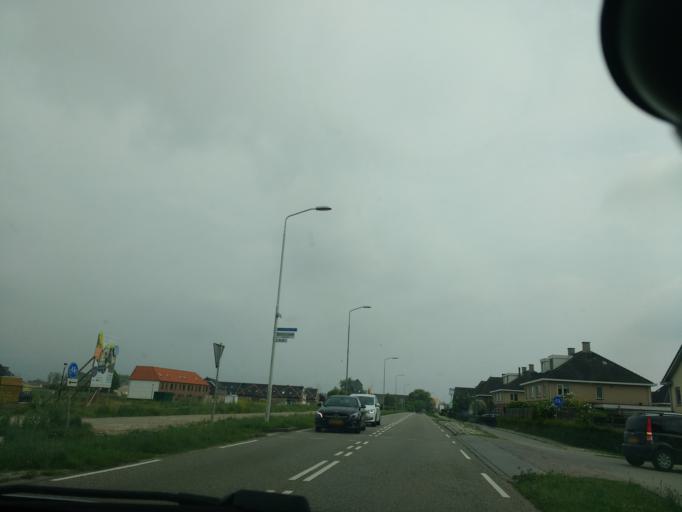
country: NL
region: Gelderland
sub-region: Gemeente Overbetuwe
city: Oosterhout
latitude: 51.8788
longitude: 5.8495
